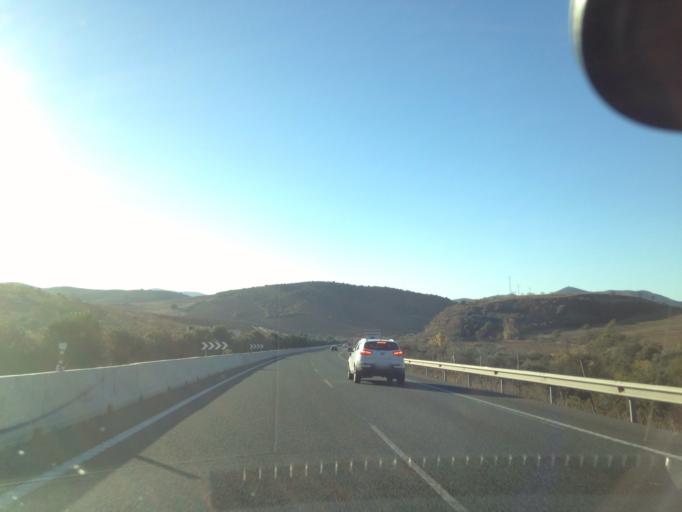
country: ES
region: Andalusia
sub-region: Provincia de Malaga
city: Casabermeja
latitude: 36.9444
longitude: -4.4404
